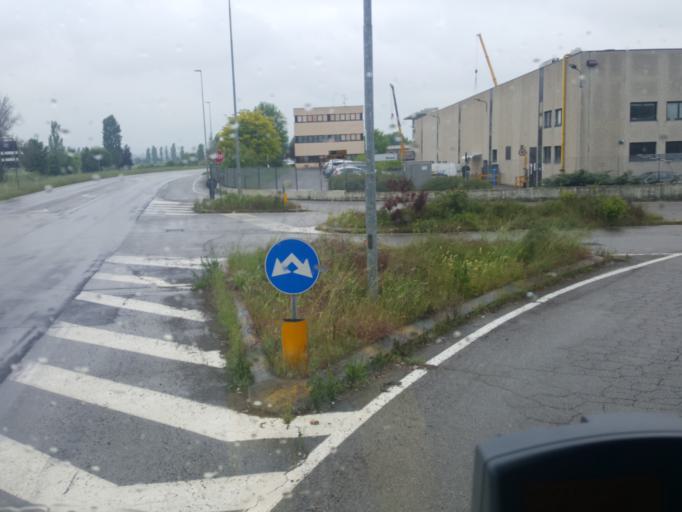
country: IT
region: Emilia-Romagna
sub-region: Provincia di Reggio Emilia
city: Codemondo-Quaresimo
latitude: 44.7172
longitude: 10.5581
